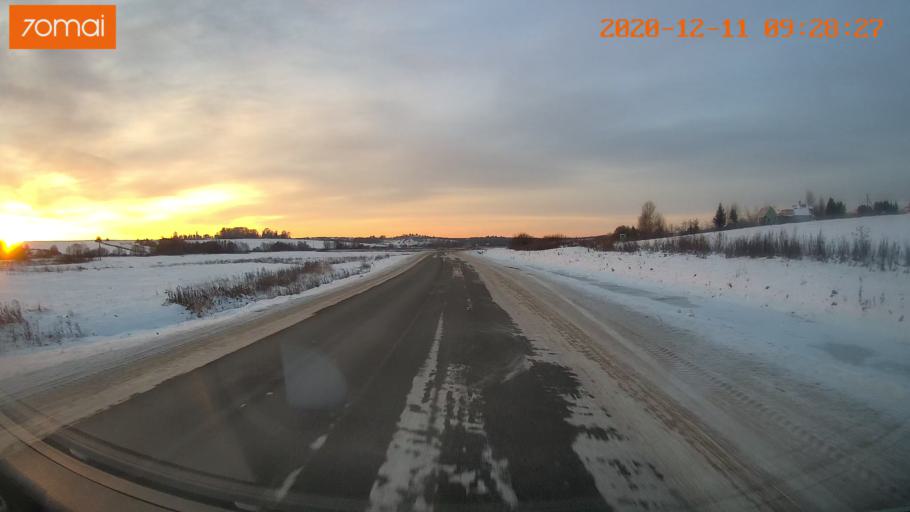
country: RU
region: Vologda
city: Vologda
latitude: 59.1530
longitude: 40.0085
